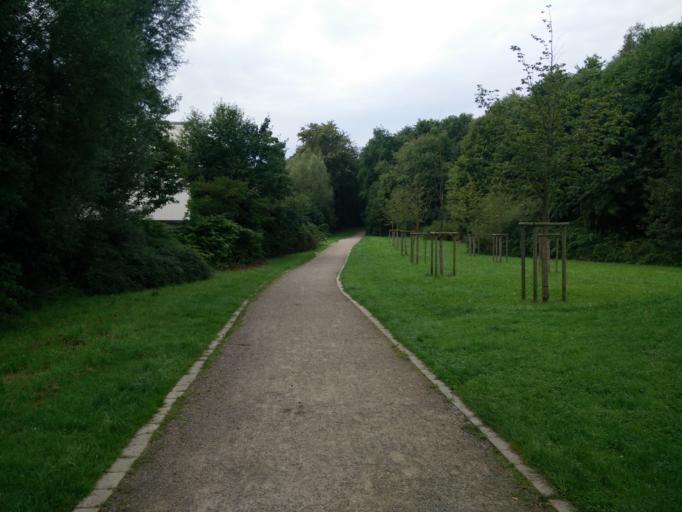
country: DE
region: North Rhine-Westphalia
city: Bochum-Hordel
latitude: 51.5059
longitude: 7.1830
